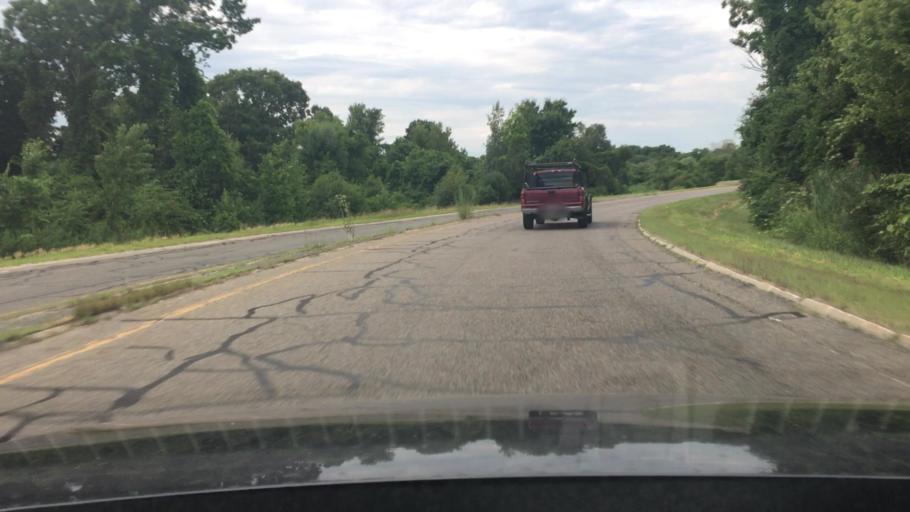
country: US
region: Massachusetts
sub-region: Essex County
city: Danvers
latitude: 42.5603
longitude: -70.9725
